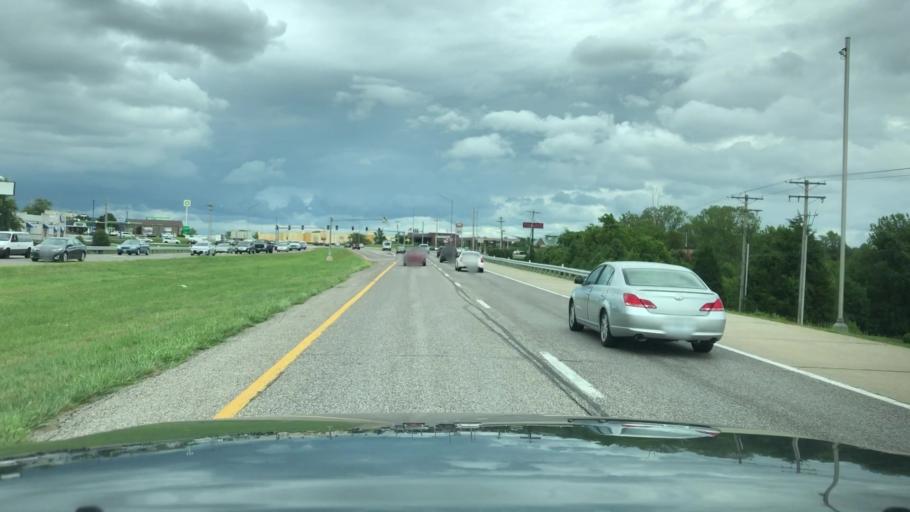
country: US
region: Missouri
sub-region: Saint Charles County
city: Saint Charles
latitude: 38.7600
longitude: -90.5327
